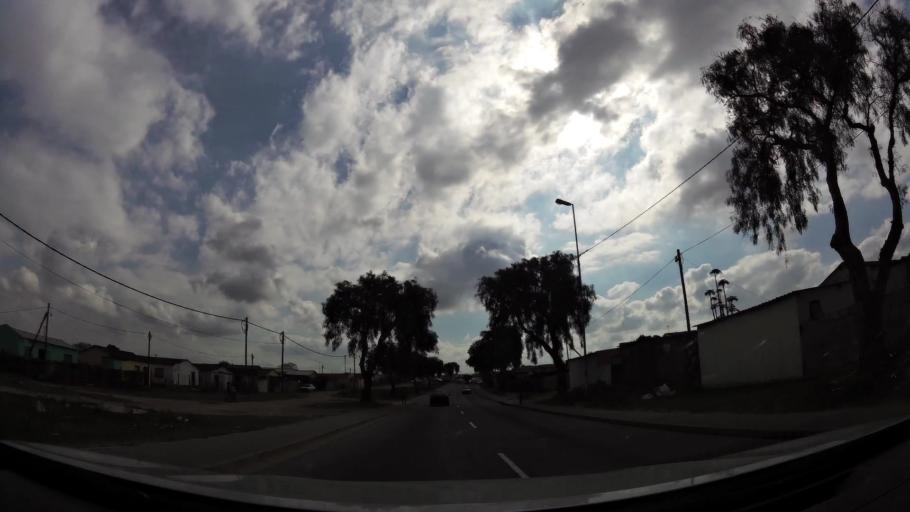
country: ZA
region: Eastern Cape
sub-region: Nelson Mandela Bay Metropolitan Municipality
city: Port Elizabeth
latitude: -33.8036
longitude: 25.5883
